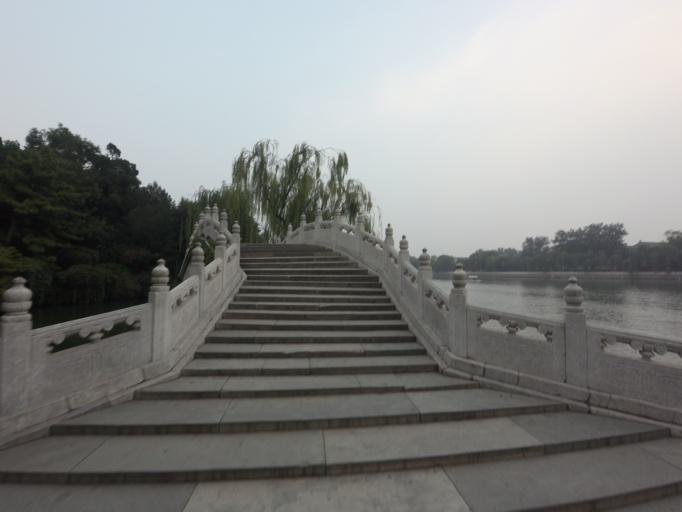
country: CN
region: Beijing
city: Jingshan
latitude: 39.9239
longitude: 116.3815
